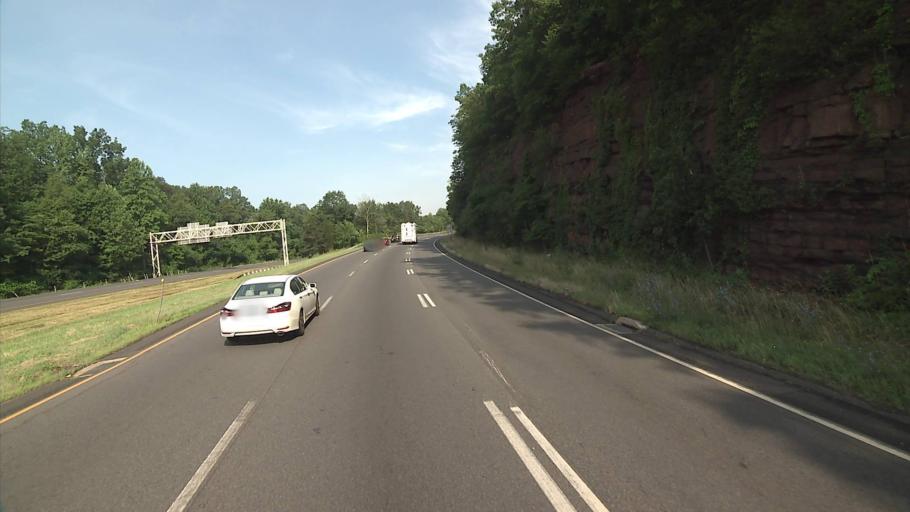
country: US
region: Connecticut
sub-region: New Haven County
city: Meriden
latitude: 41.5486
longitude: -72.8259
